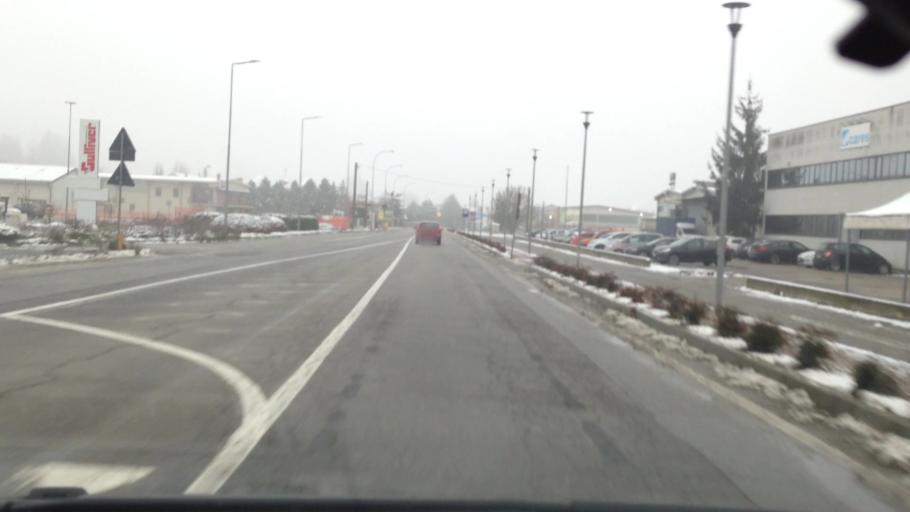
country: IT
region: Piedmont
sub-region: Provincia di Asti
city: Montegrosso
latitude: 44.8209
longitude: 8.2298
